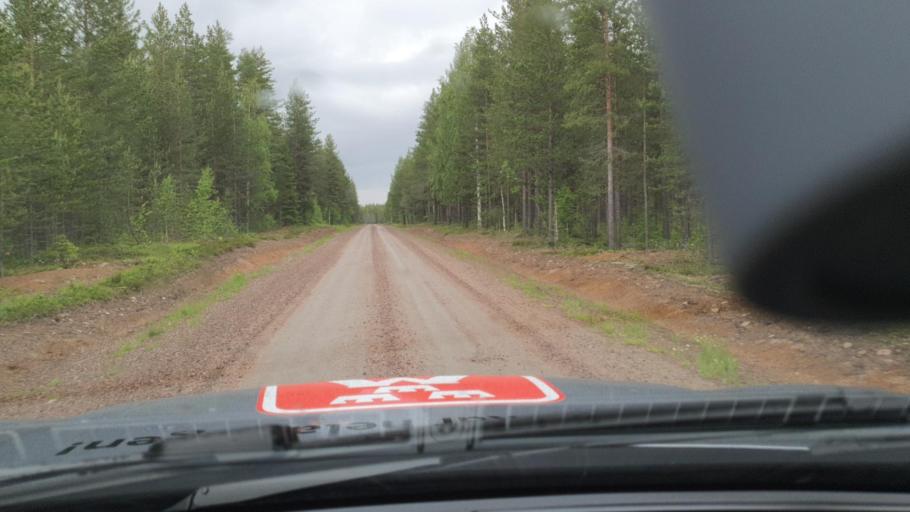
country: SE
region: Norrbotten
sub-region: Overkalix Kommun
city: OEverkalix
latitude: 66.6189
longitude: 22.7289
